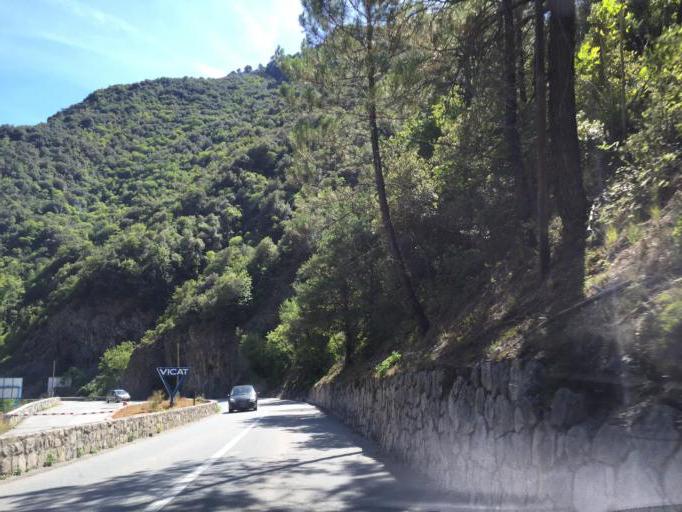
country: FR
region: Provence-Alpes-Cote d'Azur
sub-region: Departement des Alpes-Maritimes
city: Levens
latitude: 43.9233
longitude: 7.1860
